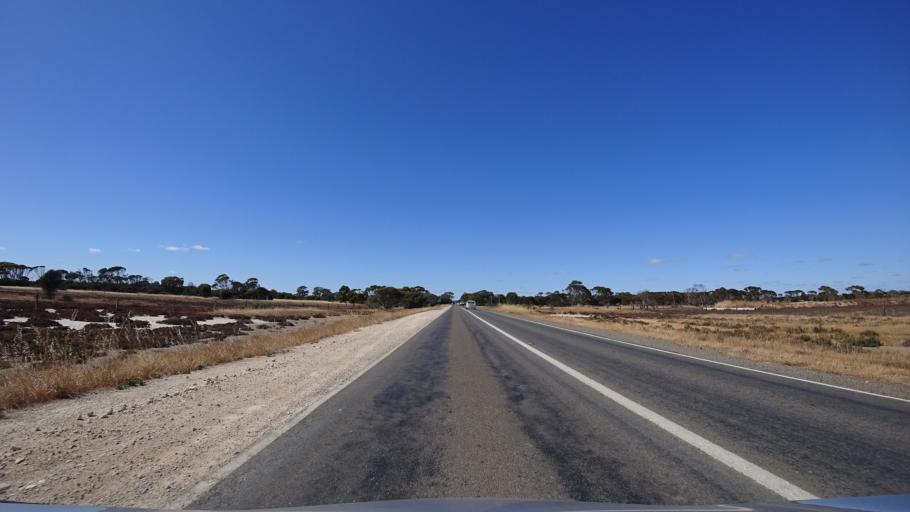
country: AU
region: South Australia
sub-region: Kangaroo Island
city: Kingscote
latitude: -35.6795
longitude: 137.5733
